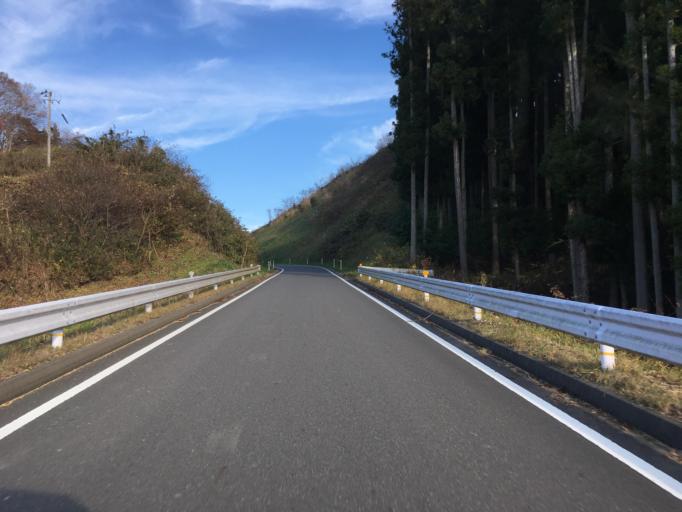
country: JP
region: Fukushima
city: Ishikawa
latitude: 37.2338
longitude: 140.5845
